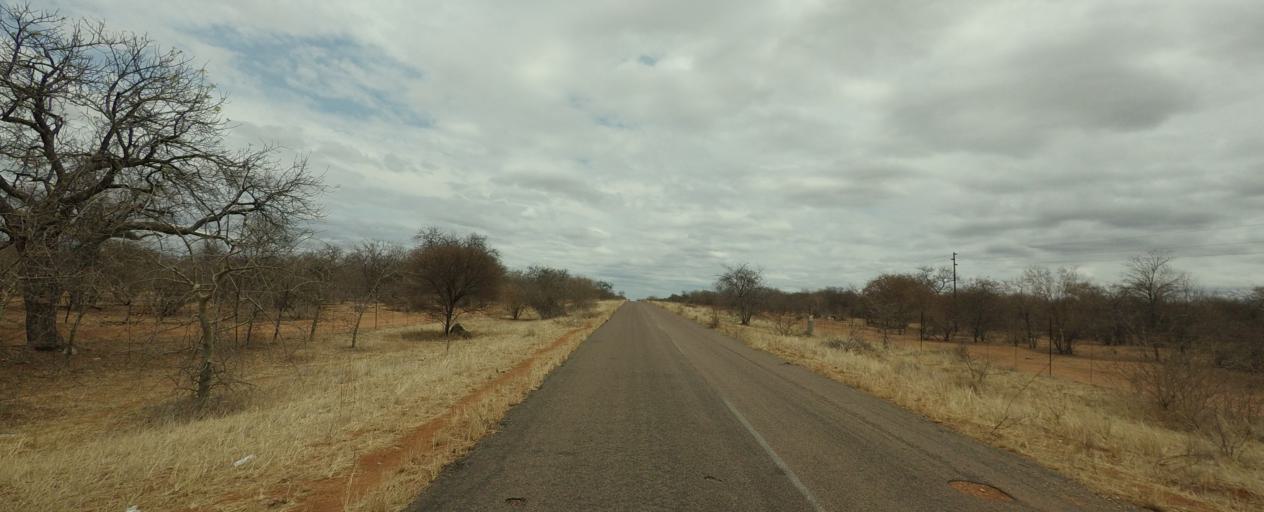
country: BW
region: Central
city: Mathathane
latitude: -22.6575
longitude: 28.7169
